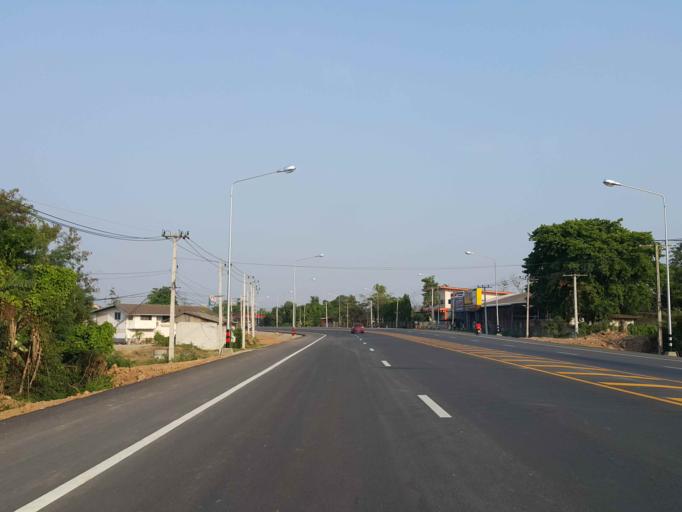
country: TH
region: Sukhothai
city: Sawankhalok
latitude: 17.3039
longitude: 99.8228
